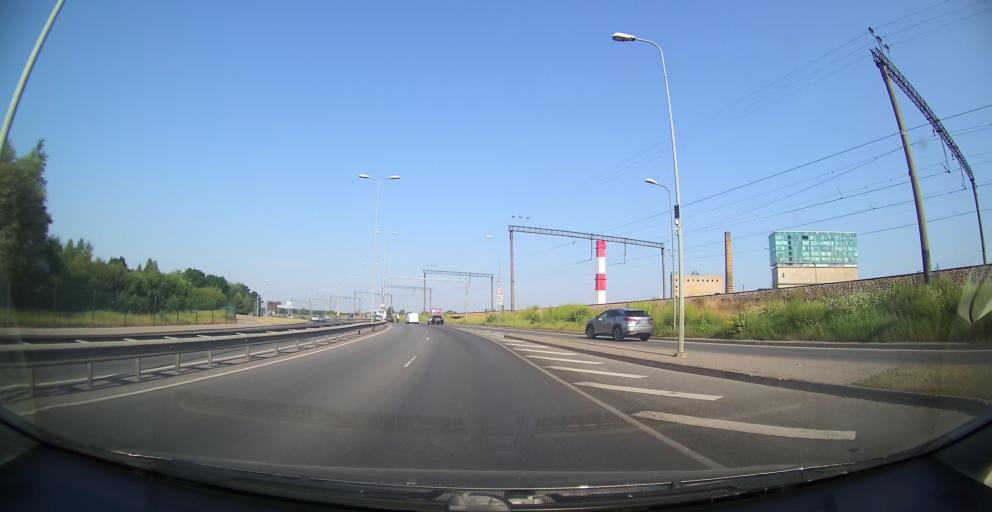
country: EE
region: Harju
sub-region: Tallinna linn
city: Tallinn
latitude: 59.4204
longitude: 24.7749
